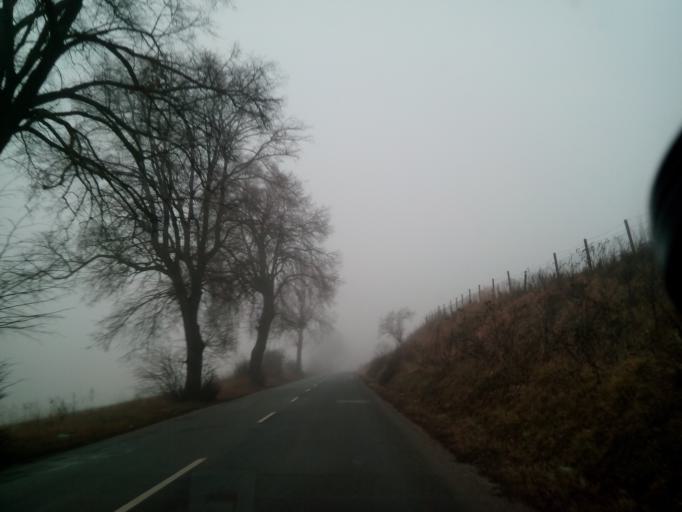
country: SK
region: Presovsky
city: Spisske Podhradie
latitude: 48.9619
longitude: 20.7884
